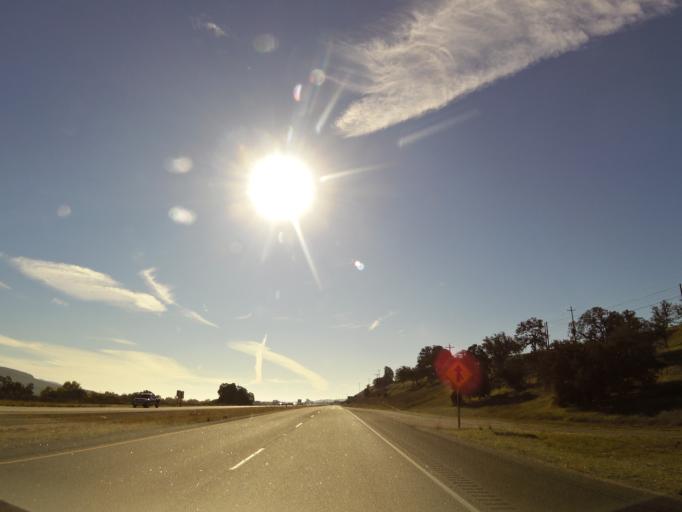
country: US
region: California
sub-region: San Luis Obispo County
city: San Miguel
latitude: 35.8131
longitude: -120.7534
